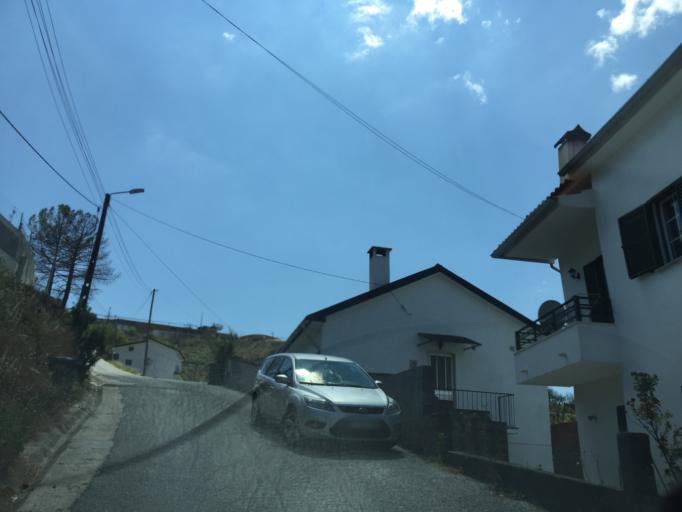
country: PT
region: Coimbra
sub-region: Pampilhosa da Serra
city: Pampilhosa da Serra
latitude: 40.0457
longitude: -7.9543
